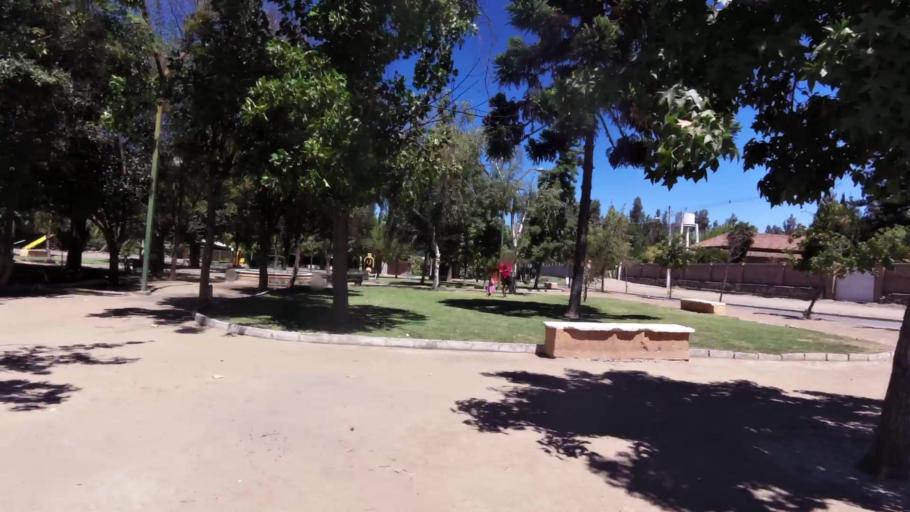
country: CL
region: O'Higgins
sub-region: Provincia de Cachapoal
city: Rancagua
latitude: -34.2277
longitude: -70.7892
